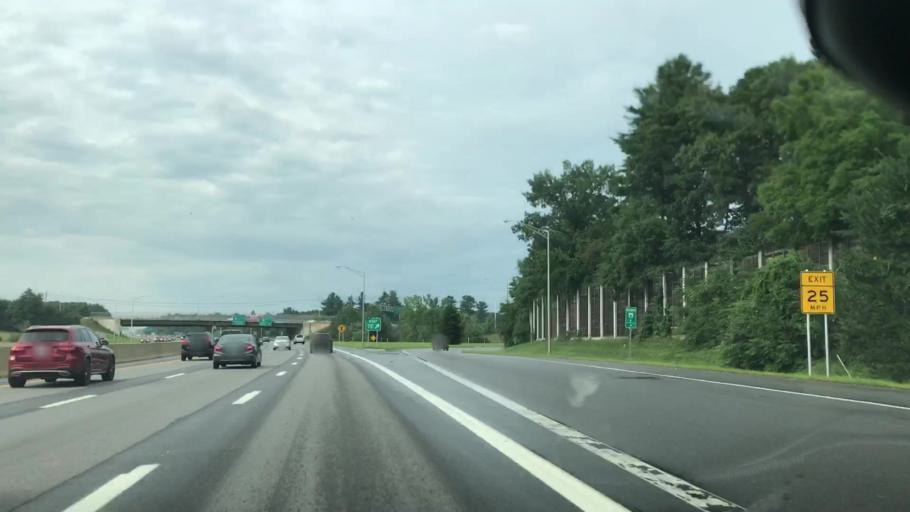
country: US
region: New Hampshire
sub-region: Hillsborough County
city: Nashua
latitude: 42.7734
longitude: -71.4928
